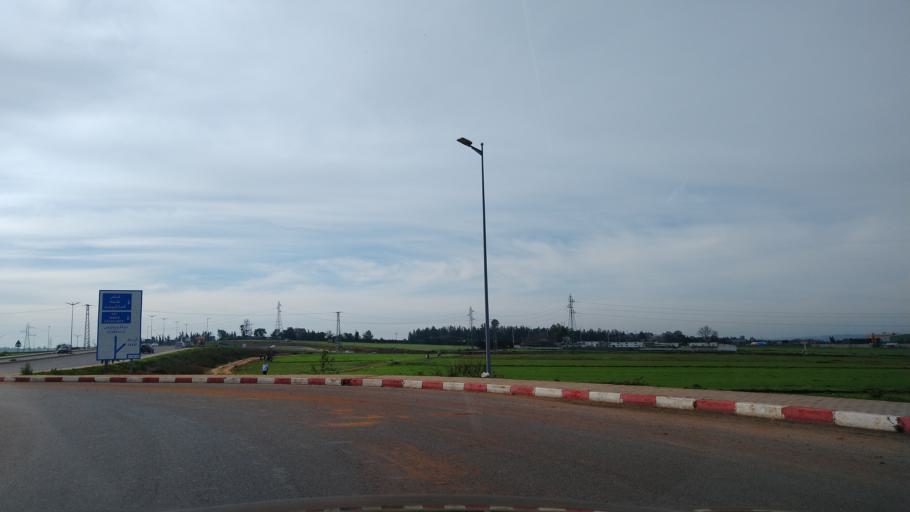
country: MA
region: Rabat-Sale-Zemmour-Zaer
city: Sale
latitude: 33.9841
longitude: -6.7402
